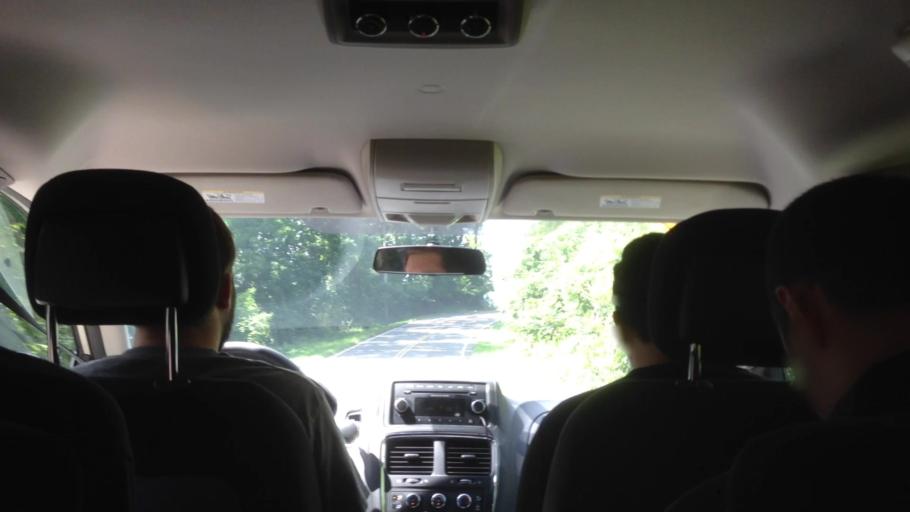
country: US
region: New York
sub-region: Dutchess County
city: Tivoli
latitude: 42.0562
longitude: -73.8963
